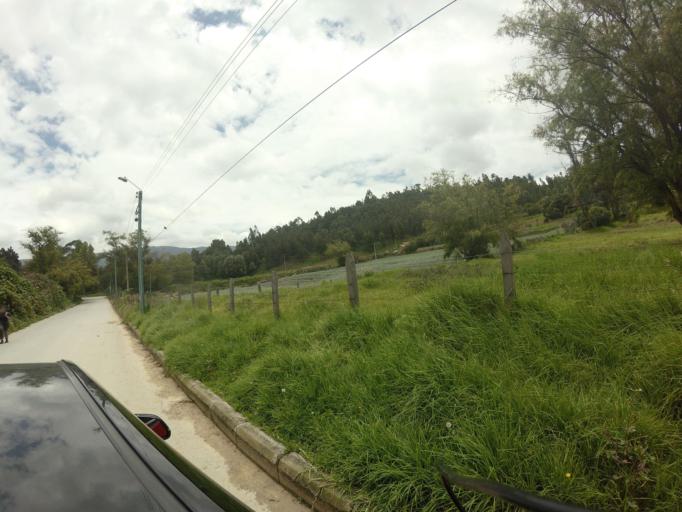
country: CO
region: Boyaca
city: Duitama
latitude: 5.8254
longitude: -73.0211
